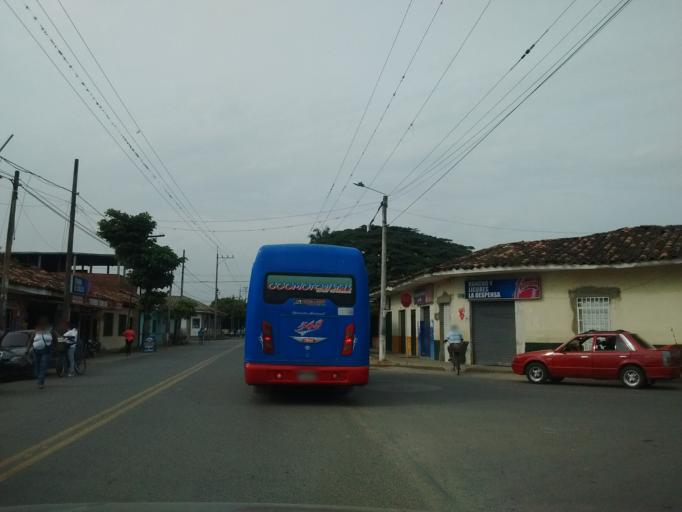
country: CO
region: Cauca
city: Puerto Tejada
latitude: 3.1720
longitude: -76.4576
